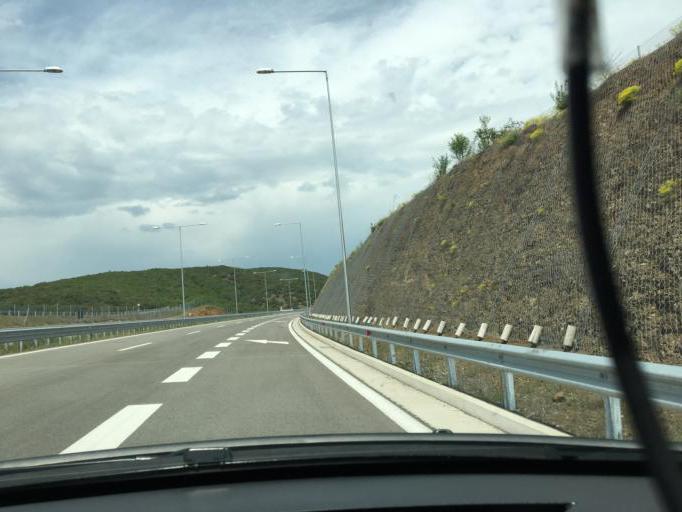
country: MK
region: Gevgelija
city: Miravci
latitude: 41.2992
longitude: 22.4296
